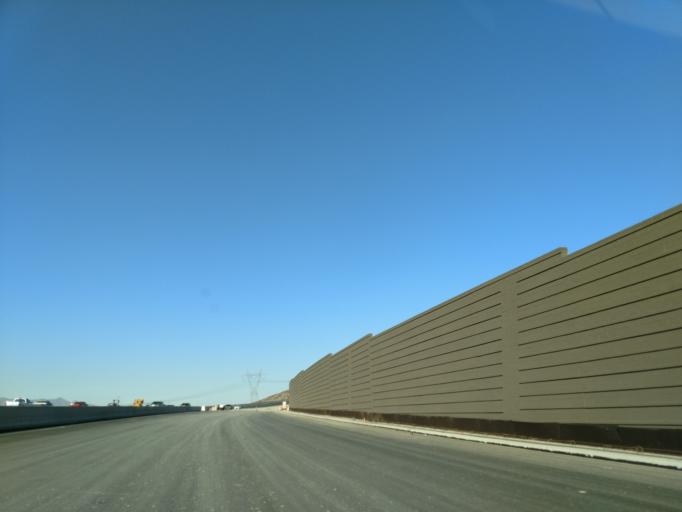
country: US
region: Arizona
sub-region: Maricopa County
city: Laveen
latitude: 33.2916
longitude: -112.1308
